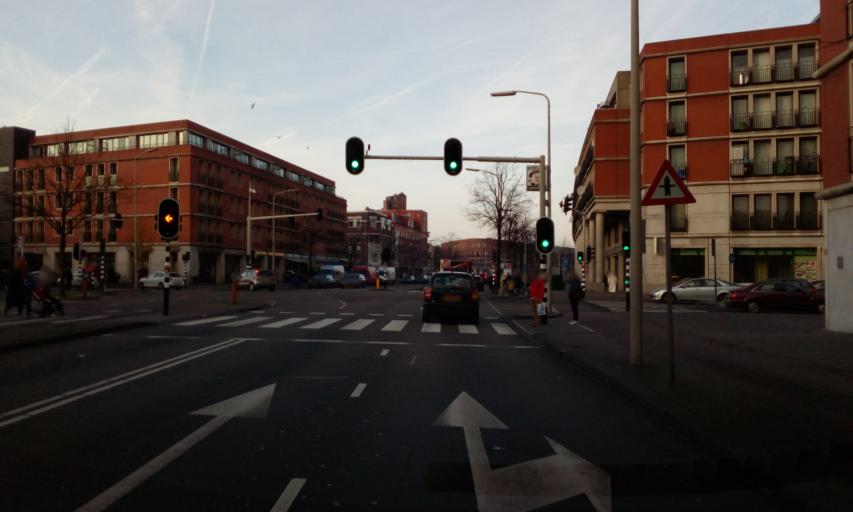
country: NL
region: South Holland
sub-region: Gemeente Den Haag
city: The Hague
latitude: 52.0650
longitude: 4.3071
